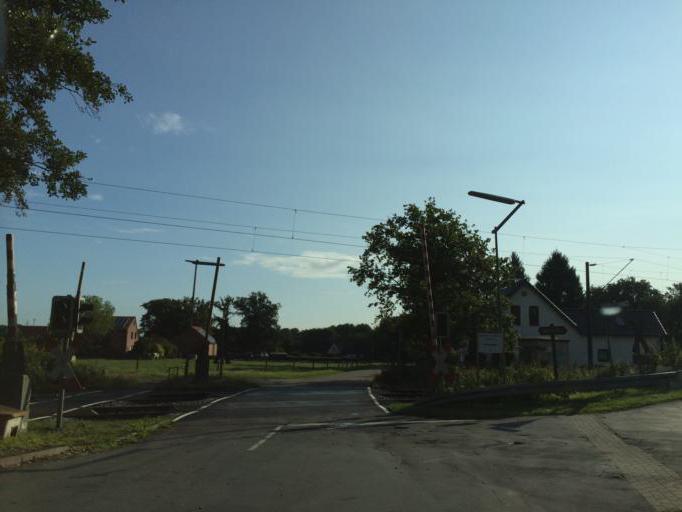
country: DE
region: Lower Saxony
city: Ganderkesee
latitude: 53.0928
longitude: 8.5641
